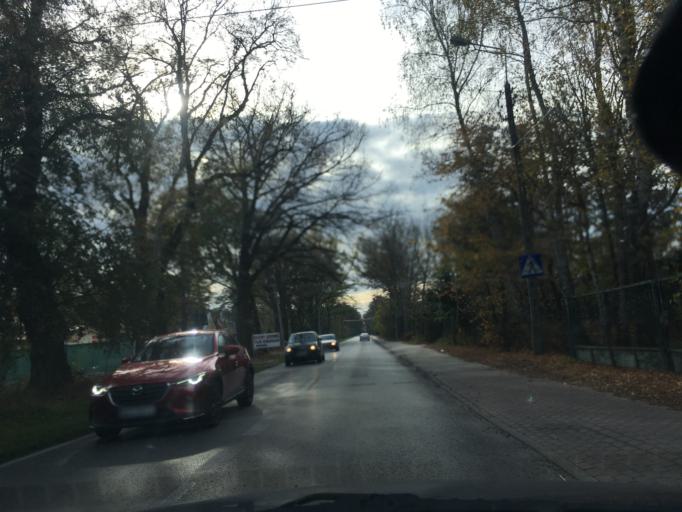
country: PL
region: Masovian Voivodeship
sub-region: Powiat piaseczynski
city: Lesznowola
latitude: 52.0264
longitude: 20.9575
